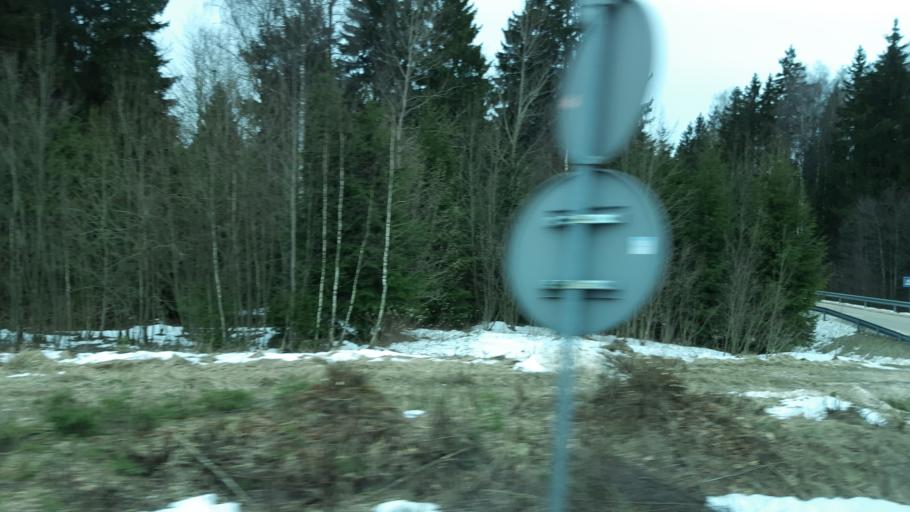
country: LT
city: Virbalis
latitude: 54.3805
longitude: 22.8173
